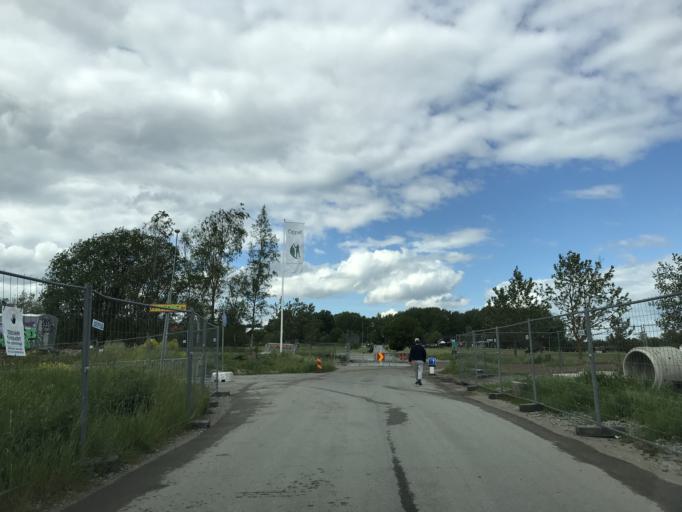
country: SE
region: Stockholm
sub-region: Solna Kommun
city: Rasunda
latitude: 59.3839
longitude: 17.9981
